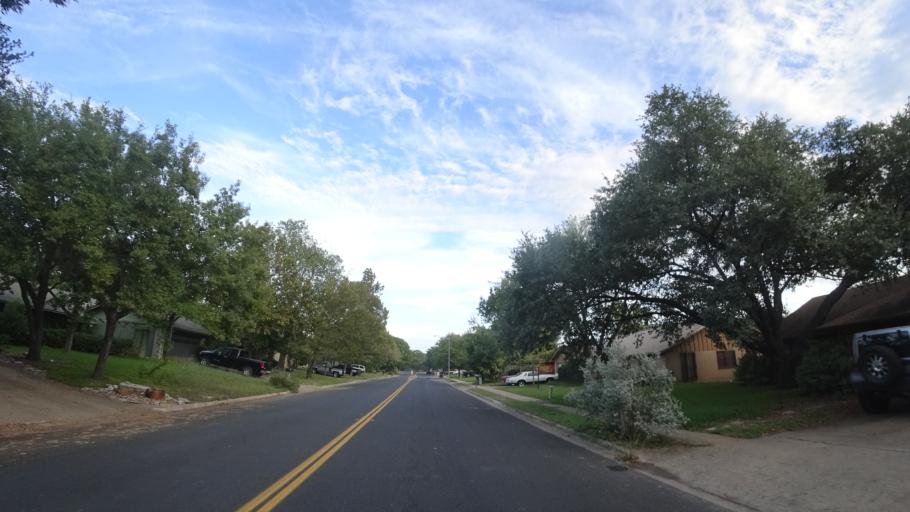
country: US
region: Texas
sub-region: Travis County
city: Austin
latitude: 30.2053
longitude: -97.7692
